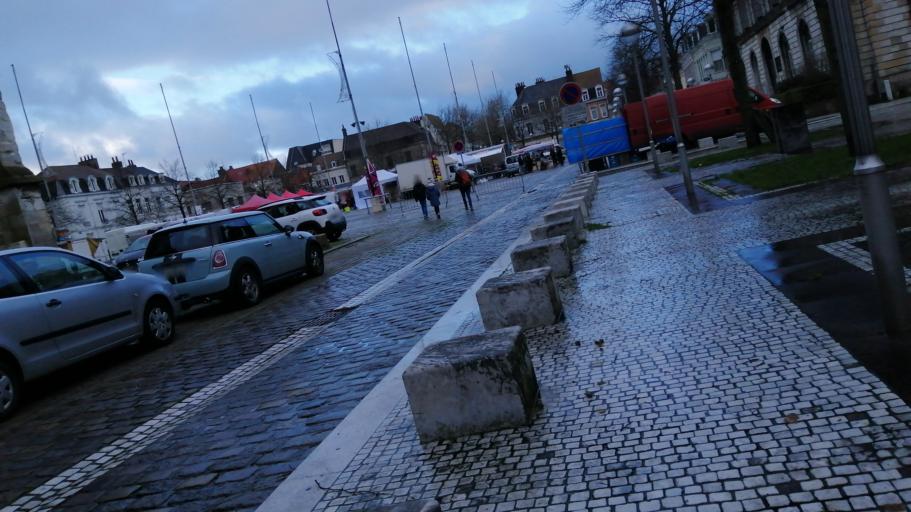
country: FR
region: Nord-Pas-de-Calais
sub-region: Departement du Pas-de-Calais
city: Calais
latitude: 50.9443
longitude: 1.8598
